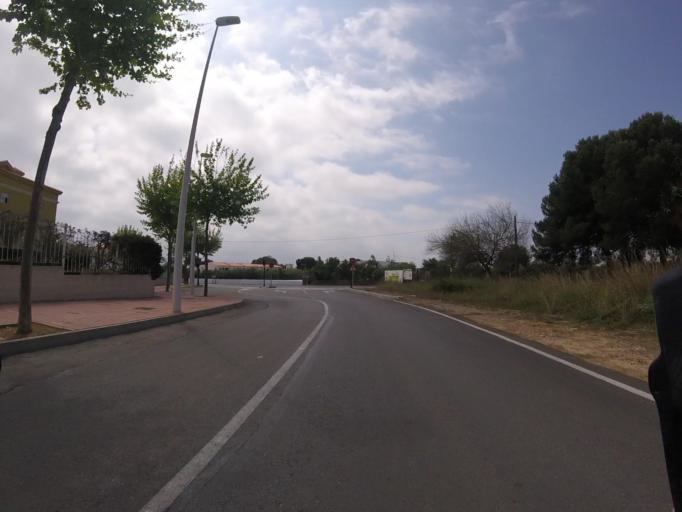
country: ES
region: Valencia
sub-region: Provincia de Castello
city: Alcoceber
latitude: 40.2448
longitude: 0.2704
